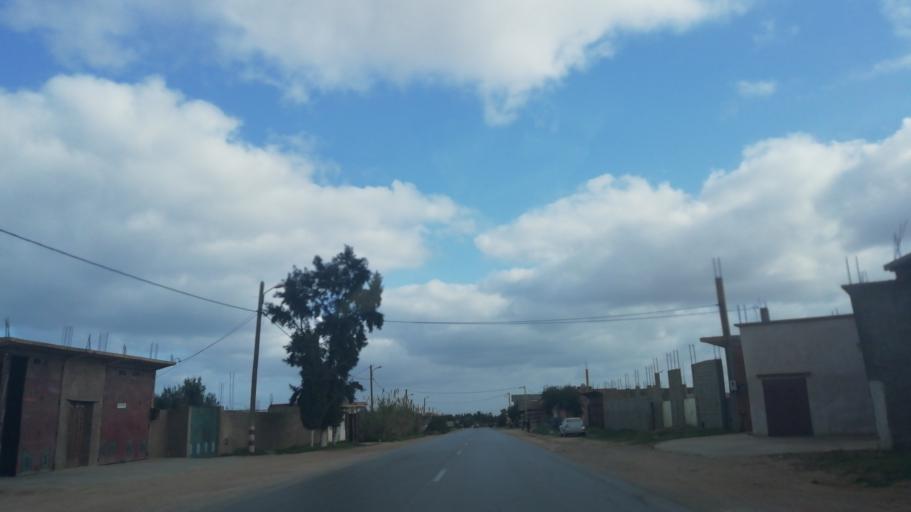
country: DZ
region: Relizane
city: Mazouna
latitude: 36.2763
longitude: 0.6360
